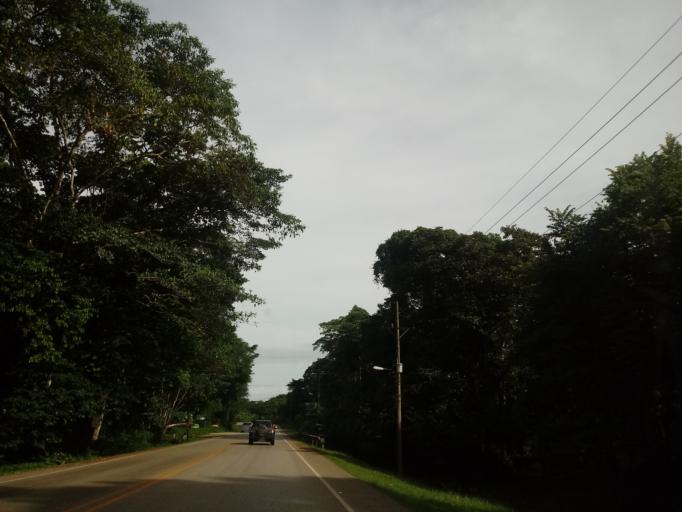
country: CR
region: San Jose
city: Daniel Flores
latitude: 9.1986
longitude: -83.7838
